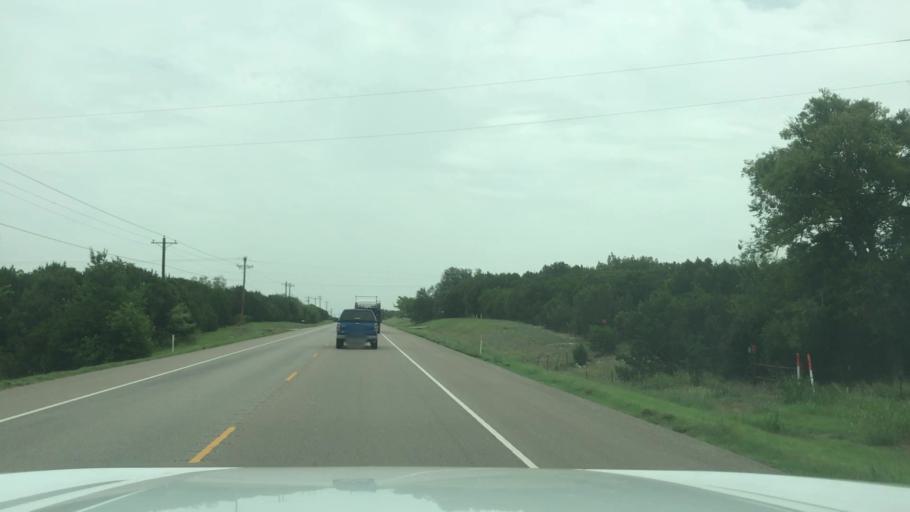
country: US
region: Texas
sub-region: Bosque County
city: Meridian
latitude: 31.9354
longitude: -97.7017
